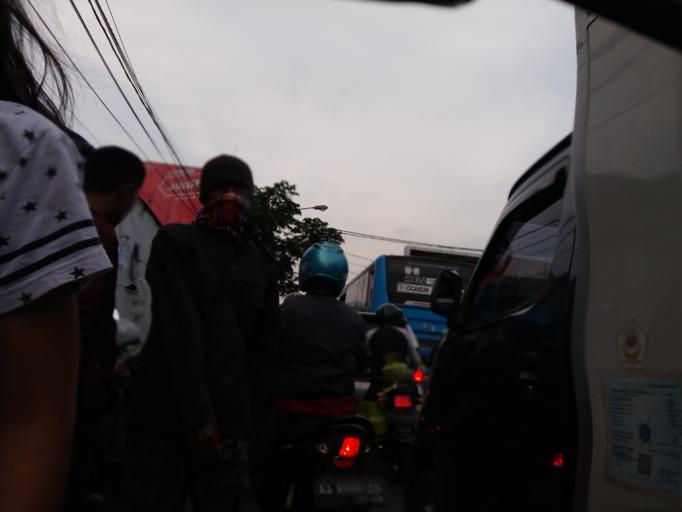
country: ID
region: West Java
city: Bandung
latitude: -6.9089
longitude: 107.6429
